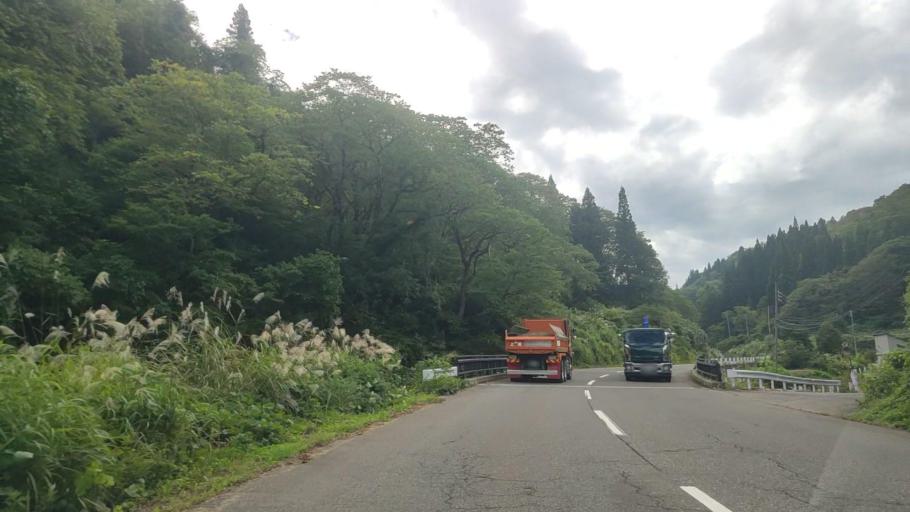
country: JP
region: Nagano
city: Iiyama
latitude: 36.8960
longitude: 138.3212
